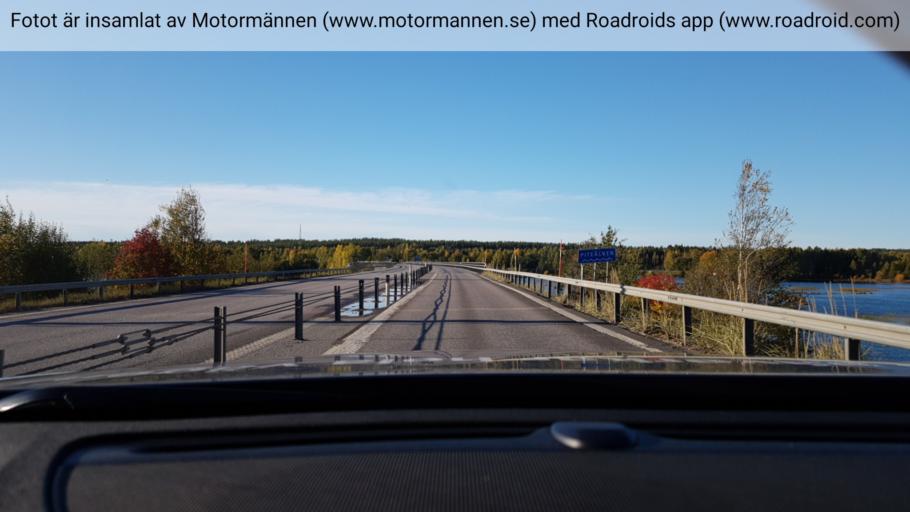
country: SE
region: Norrbotten
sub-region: Pitea Kommun
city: Bergsviken
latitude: 65.3159
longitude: 21.4131
